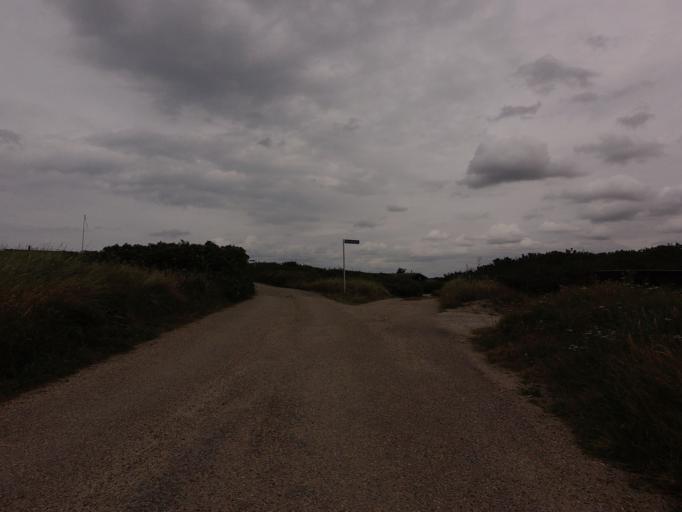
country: DK
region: North Denmark
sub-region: Jammerbugt Kommune
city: Pandrup
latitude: 57.3115
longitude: 9.6535
